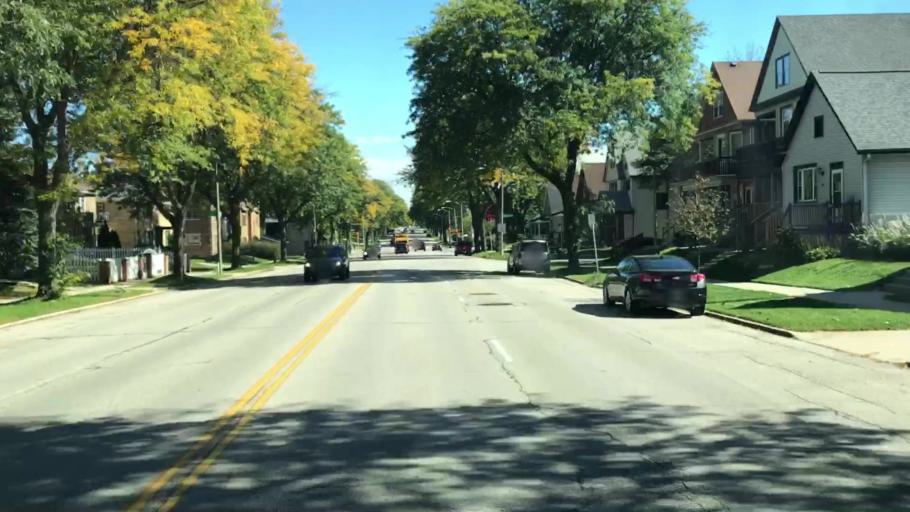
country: US
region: Wisconsin
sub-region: Milwaukee County
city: Saint Francis
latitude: 42.9883
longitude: -87.9066
